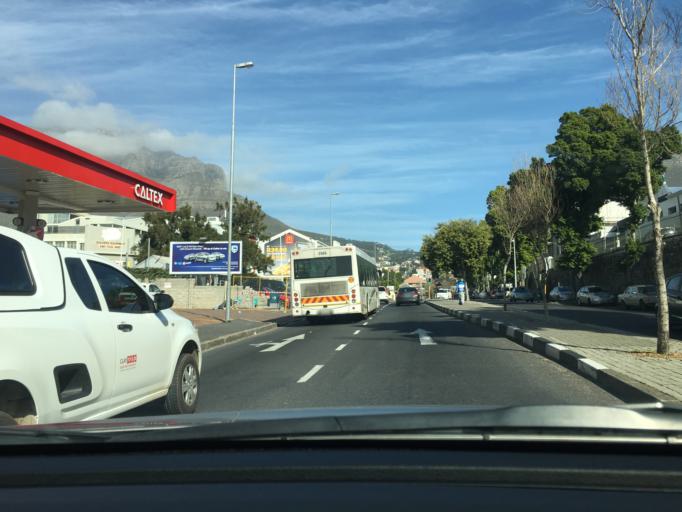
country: ZA
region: Western Cape
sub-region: City of Cape Town
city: Cape Town
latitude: -33.9252
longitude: 18.4125
